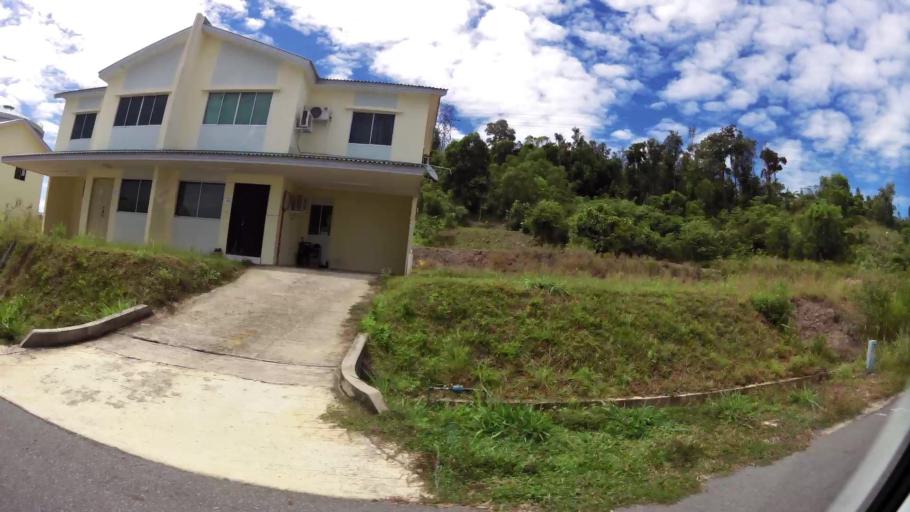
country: BN
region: Brunei and Muara
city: Bandar Seri Begawan
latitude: 4.9706
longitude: 115.0075
